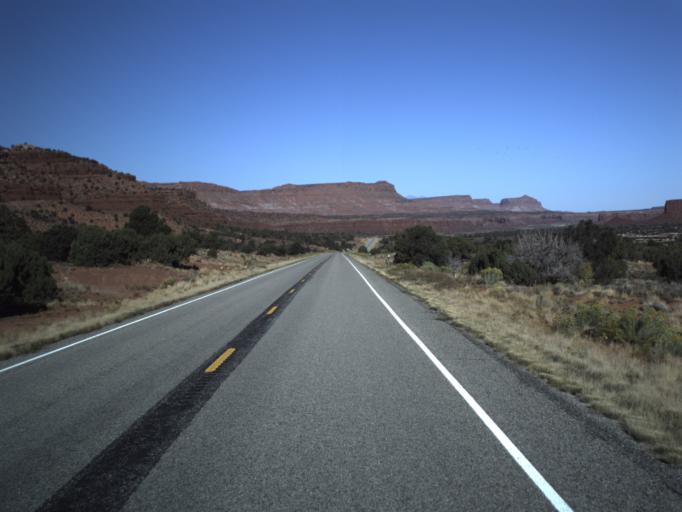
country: US
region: Utah
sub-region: San Juan County
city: Blanding
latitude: 37.6642
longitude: -110.1915
